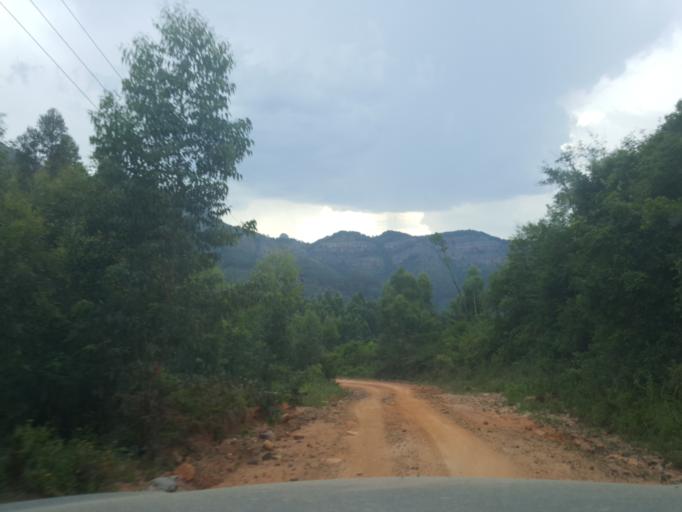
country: ZA
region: Limpopo
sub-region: Mopani District Municipality
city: Hoedspruit
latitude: -24.5917
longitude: 30.8711
